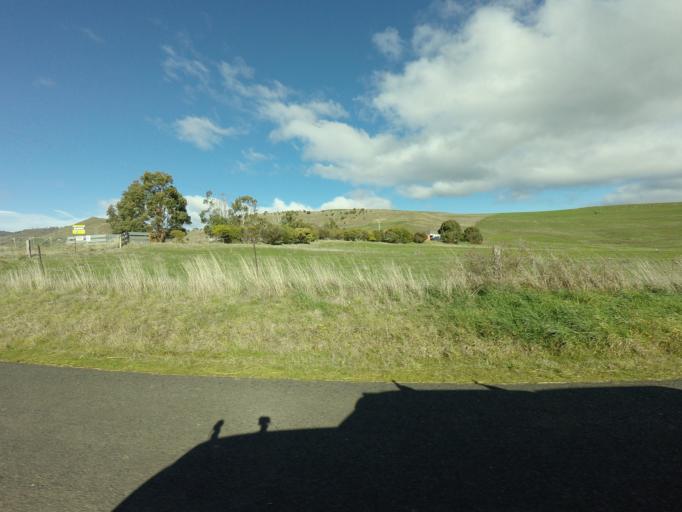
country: AU
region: Tasmania
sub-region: Derwent Valley
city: New Norfolk
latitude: -42.6948
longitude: 146.9630
